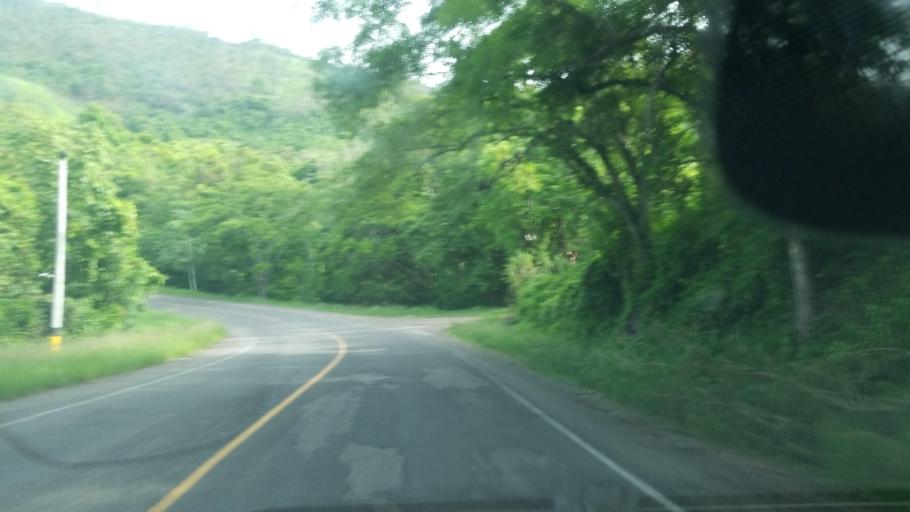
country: HN
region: Santa Barbara
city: Trinidad
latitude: 15.1324
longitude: -88.2519
